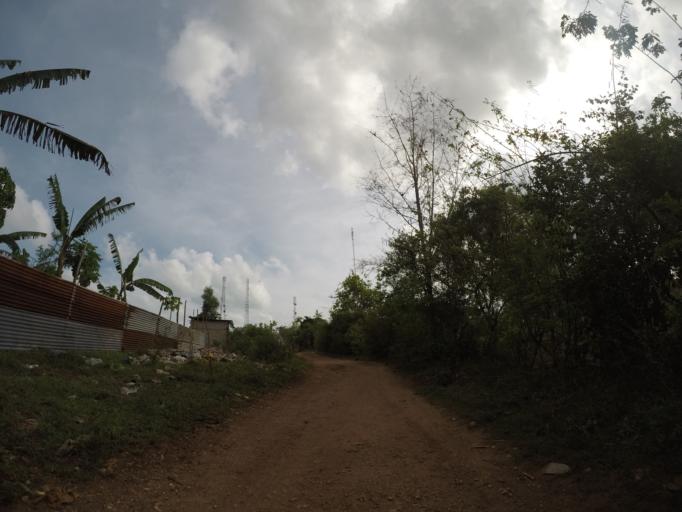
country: TZ
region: Zanzibar Central/South
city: Koani
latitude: -6.2217
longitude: 39.3195
